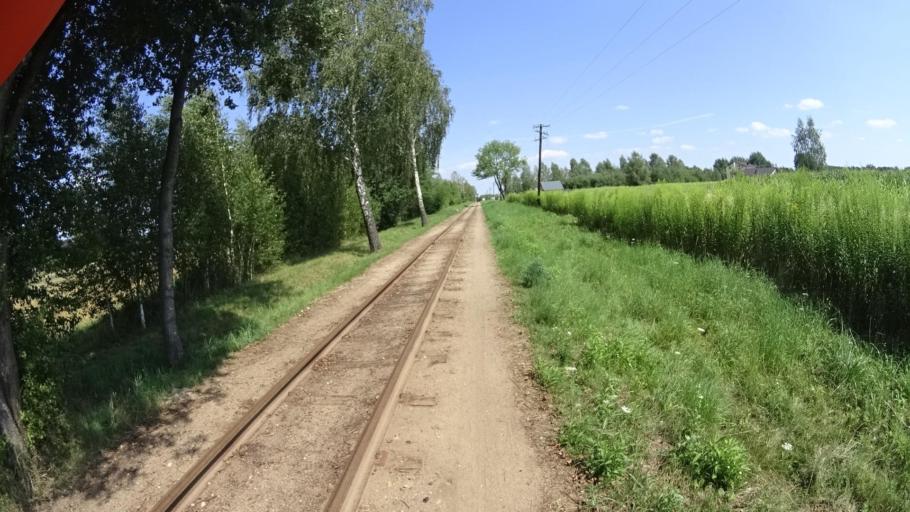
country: PL
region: Masovian Voivodeship
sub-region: Powiat piaseczynski
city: Lesznowola
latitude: 52.0215
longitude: 20.9381
